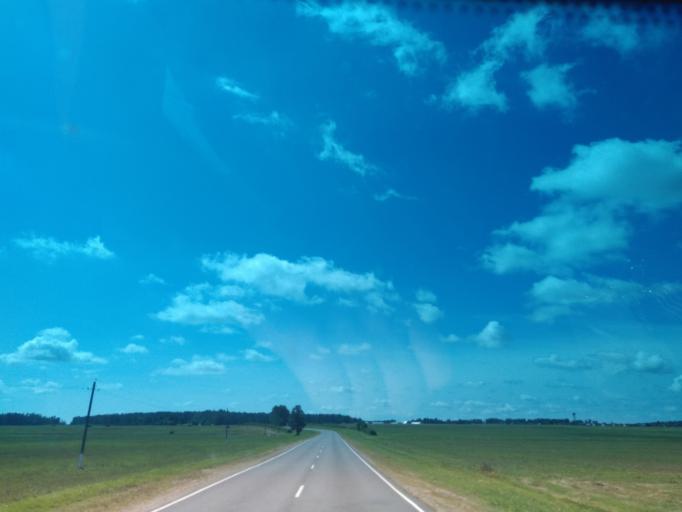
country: BY
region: Minsk
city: Uzda
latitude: 53.3651
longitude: 27.2286
